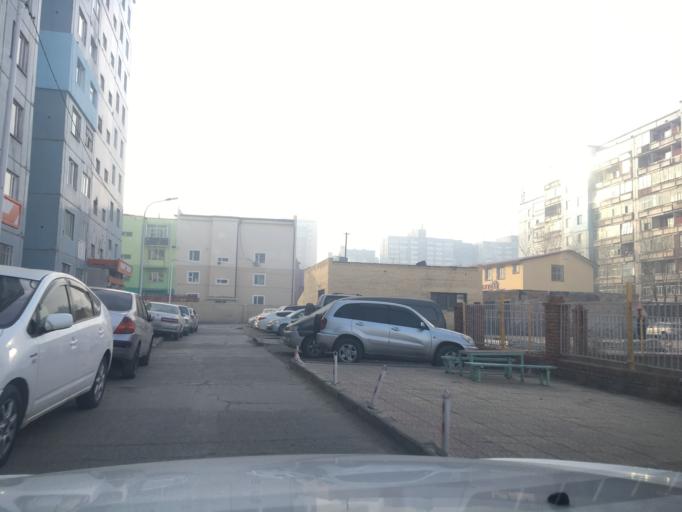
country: MN
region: Ulaanbaatar
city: Ulaanbaatar
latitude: 47.9157
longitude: 106.8698
